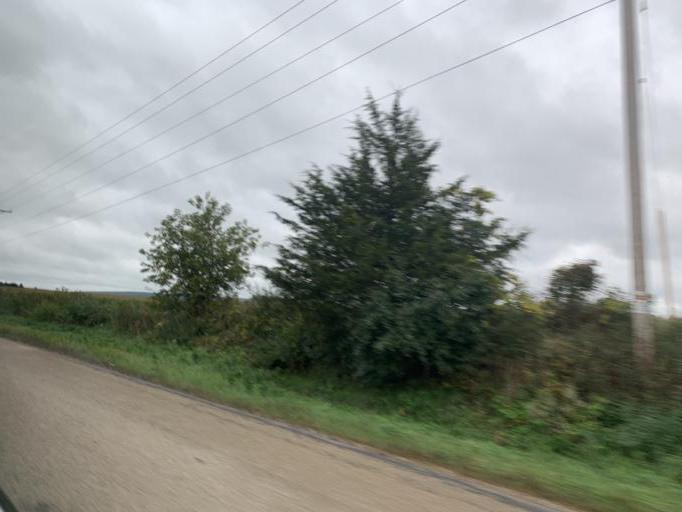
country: US
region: Wisconsin
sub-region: Sauk County
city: Prairie du Sac
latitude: 43.3429
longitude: -89.7661
